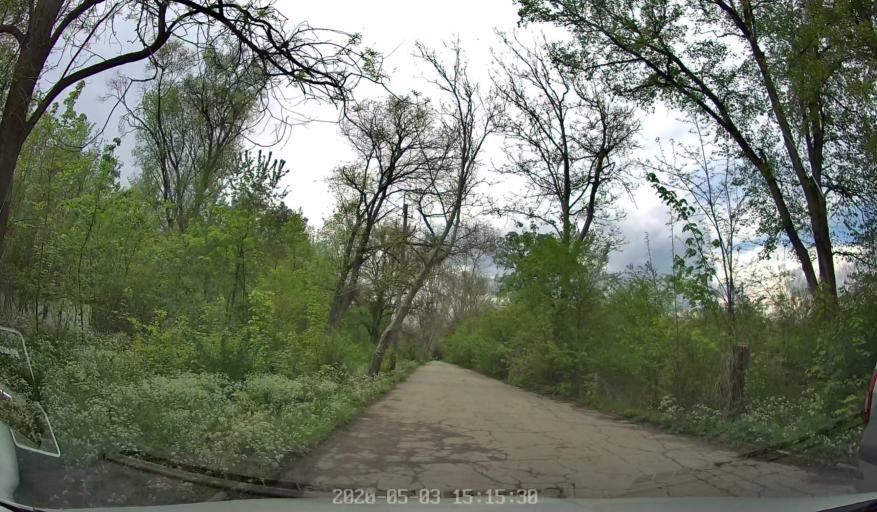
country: MD
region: Chisinau
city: Vatra
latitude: 47.0837
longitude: 28.7182
